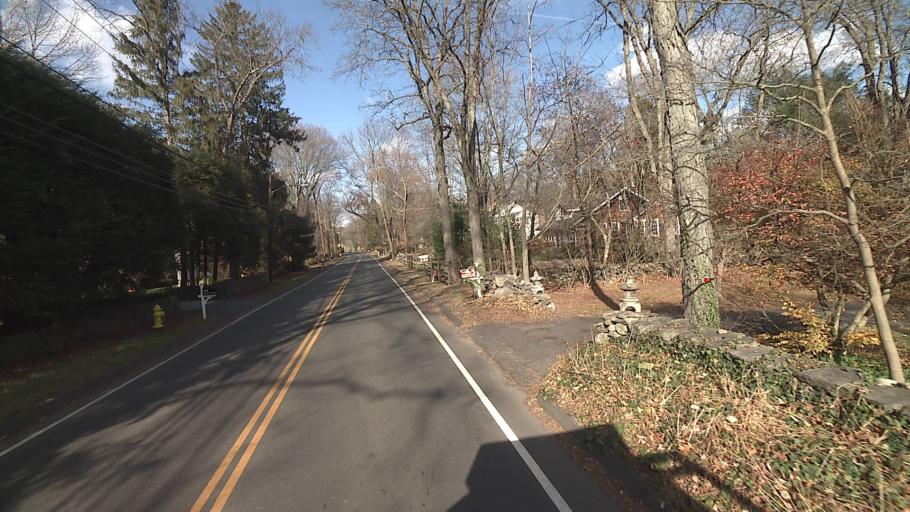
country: US
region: Connecticut
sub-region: Fairfield County
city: Westport
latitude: 41.1536
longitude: -73.3931
